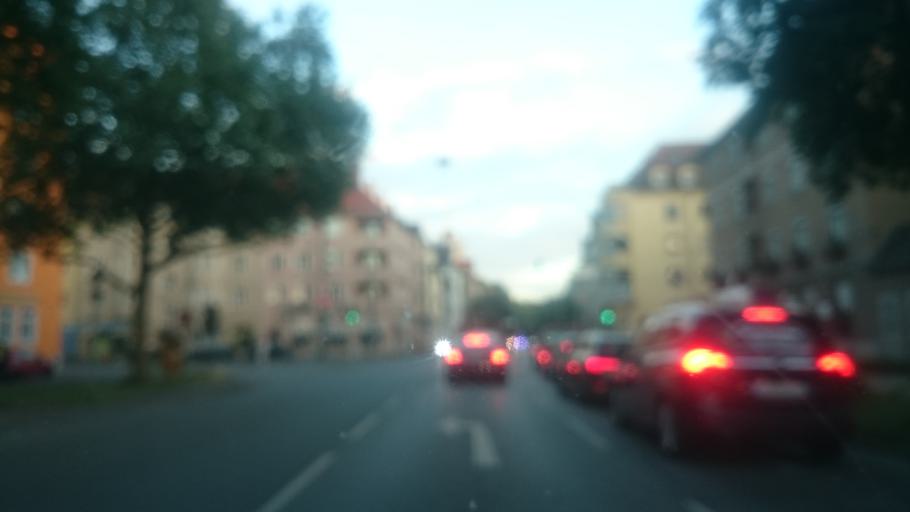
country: DE
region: Bavaria
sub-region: Swabia
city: Augsburg
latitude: 48.3664
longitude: 10.8813
